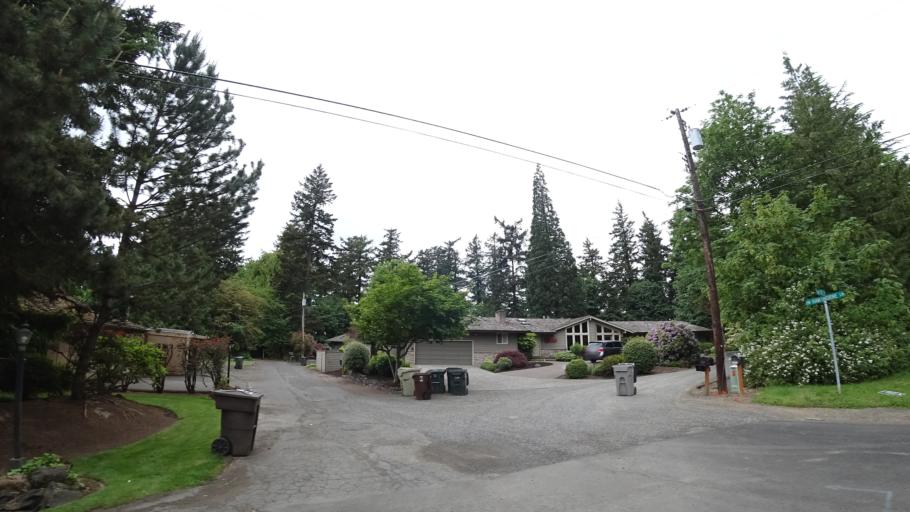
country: US
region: Oregon
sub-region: Washington County
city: Cedar Hills
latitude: 45.5002
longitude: -122.7870
